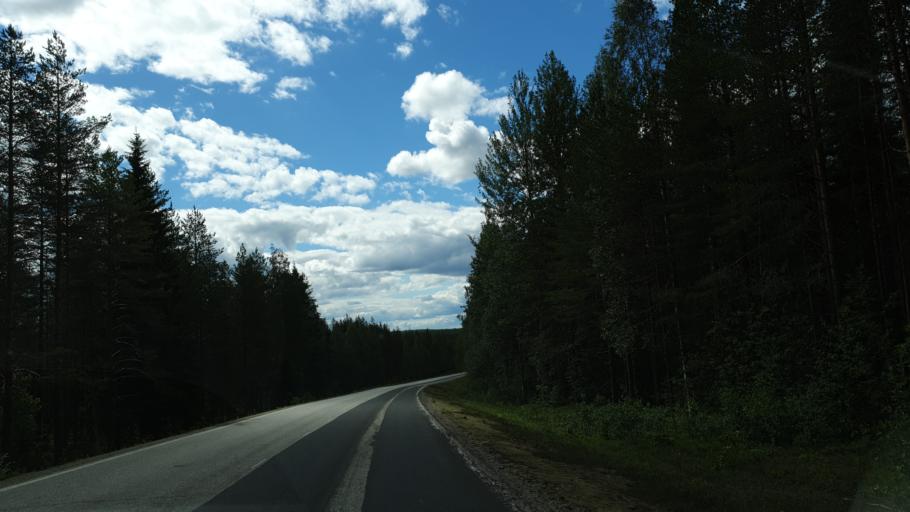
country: FI
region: Kainuu
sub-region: Kehys-Kainuu
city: Kuhmo
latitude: 63.9441
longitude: 29.6138
